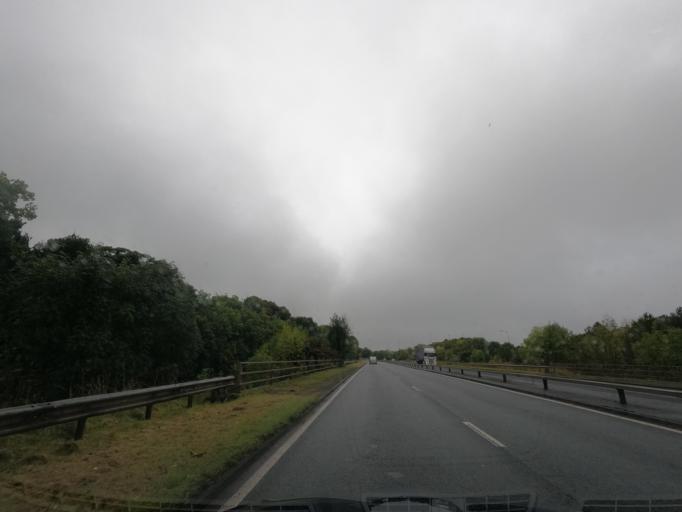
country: GB
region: England
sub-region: Redcar and Cleveland
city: South Bank
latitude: 54.5731
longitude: -1.1045
